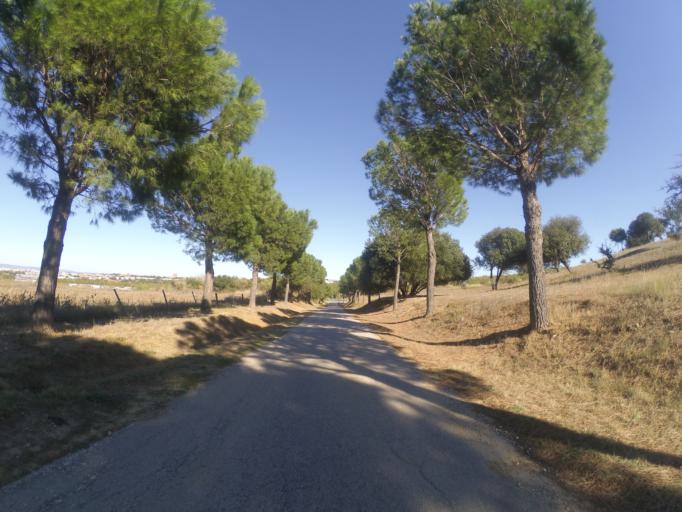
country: FR
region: Languedoc-Roussillon
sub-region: Departement des Pyrenees-Orientales
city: Perpignan
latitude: 42.6731
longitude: 2.8803
